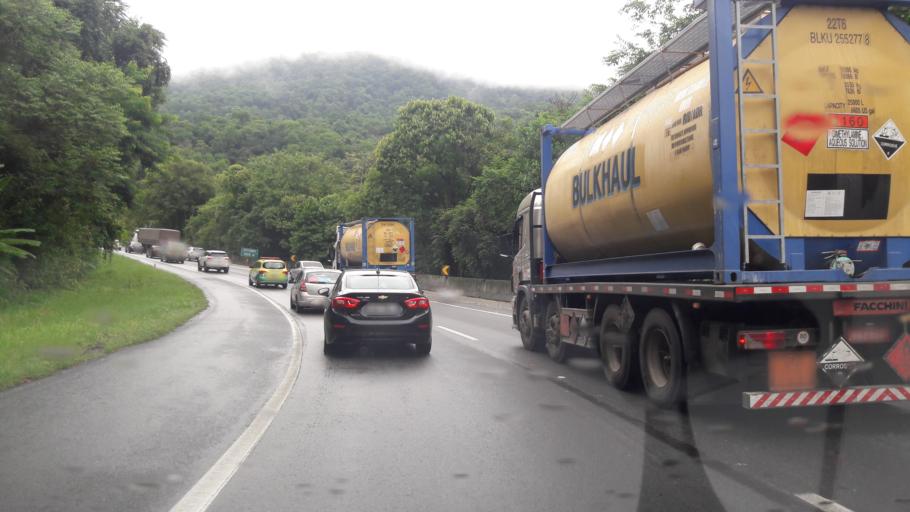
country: BR
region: Parana
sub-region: Antonina
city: Antonina
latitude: -25.5601
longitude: -48.8155
